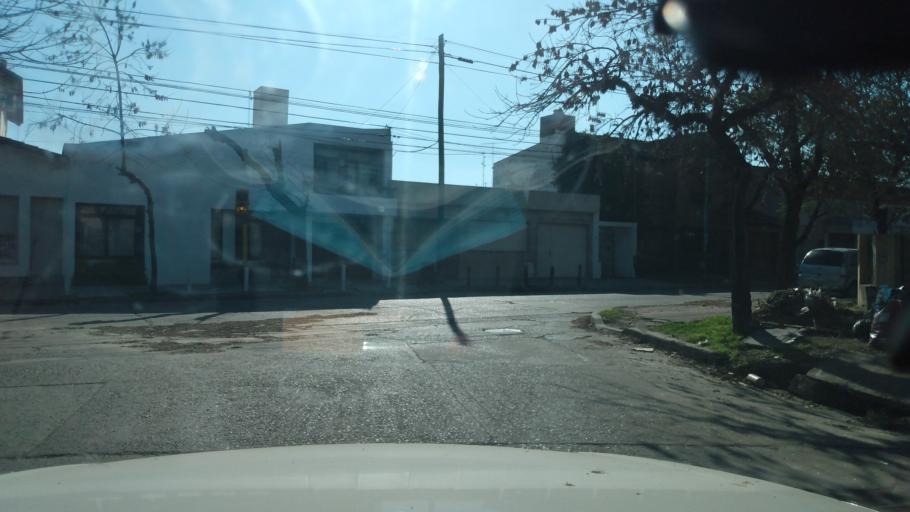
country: AR
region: Buenos Aires
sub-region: Partido de Lujan
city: Lujan
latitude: -34.5716
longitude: -59.1147
